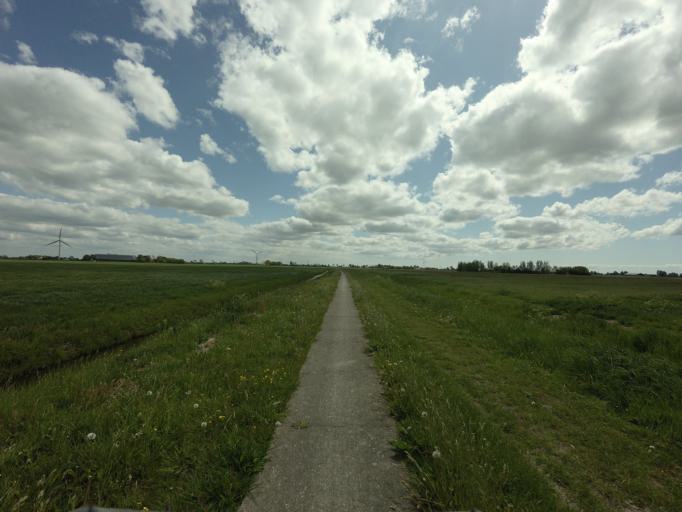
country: NL
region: Friesland
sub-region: Gemeente Franekeradeel
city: Tzum
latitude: 53.1344
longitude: 5.5732
